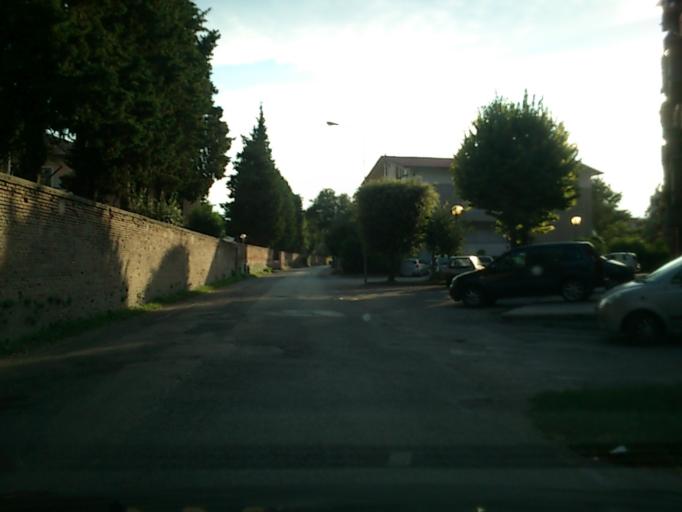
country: IT
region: The Marches
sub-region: Provincia di Pesaro e Urbino
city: Fano
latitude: 43.8389
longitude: 13.0079
